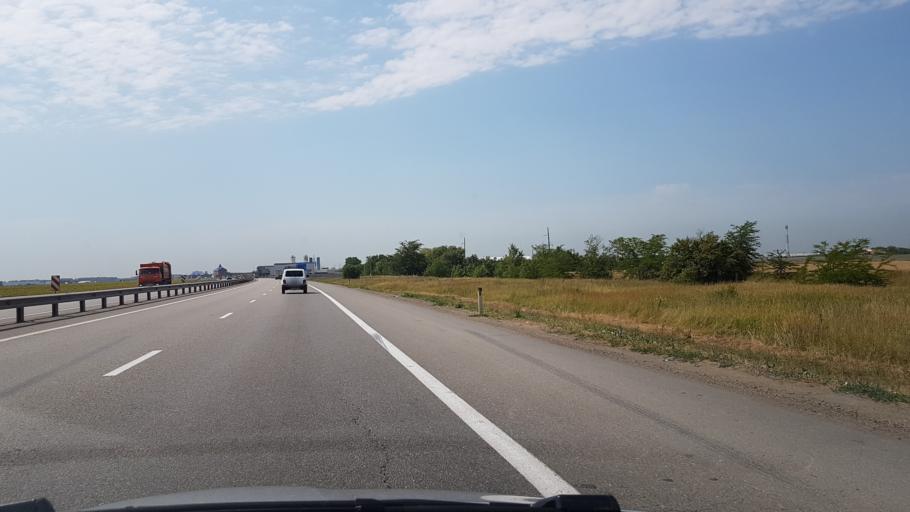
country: RU
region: Krasnodarskiy
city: Agronom
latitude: 45.1288
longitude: 39.1098
